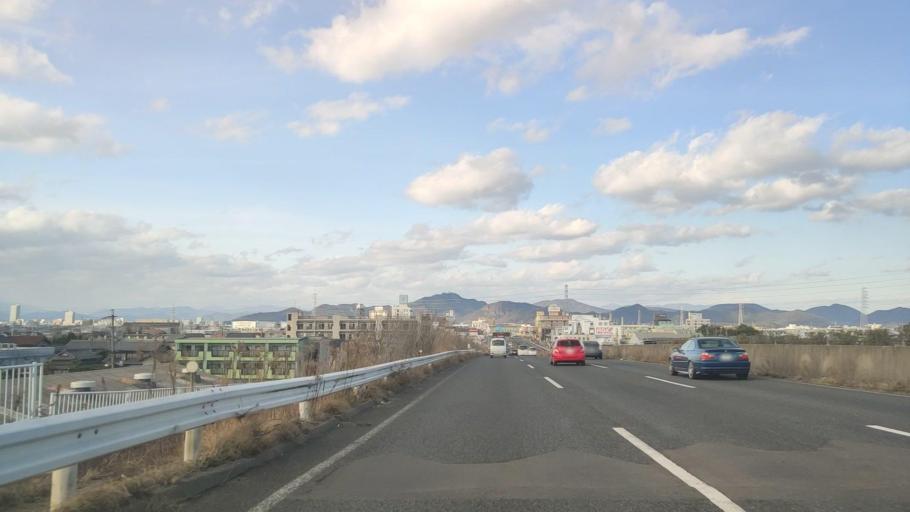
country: JP
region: Gifu
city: Kasamatsucho
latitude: 35.3750
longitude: 136.7840
